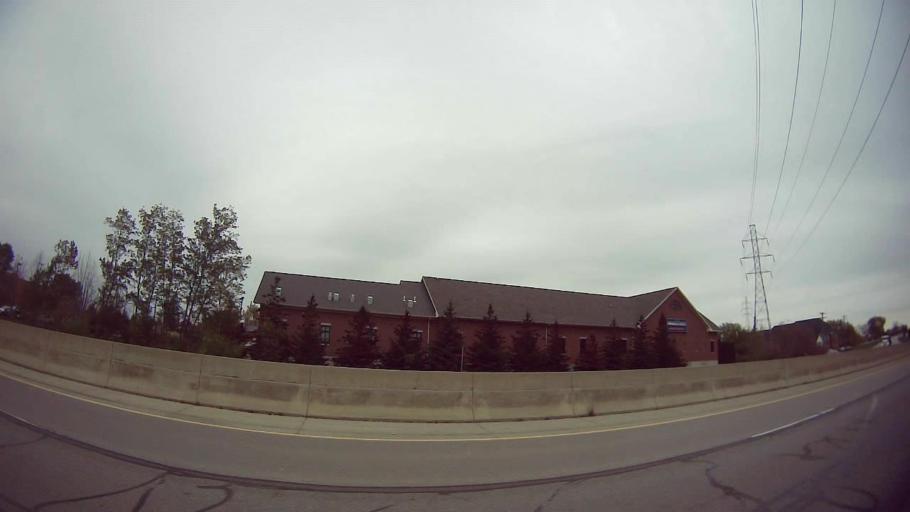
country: US
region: Michigan
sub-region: Oakland County
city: Sylvan Lake
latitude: 42.6179
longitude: -83.3197
